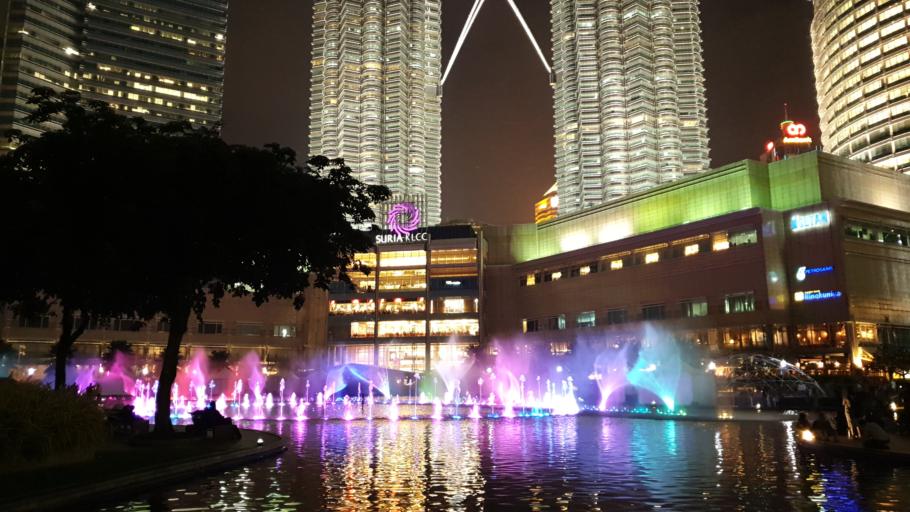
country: MY
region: Kuala Lumpur
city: Kuala Lumpur
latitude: 3.1563
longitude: 101.7136
